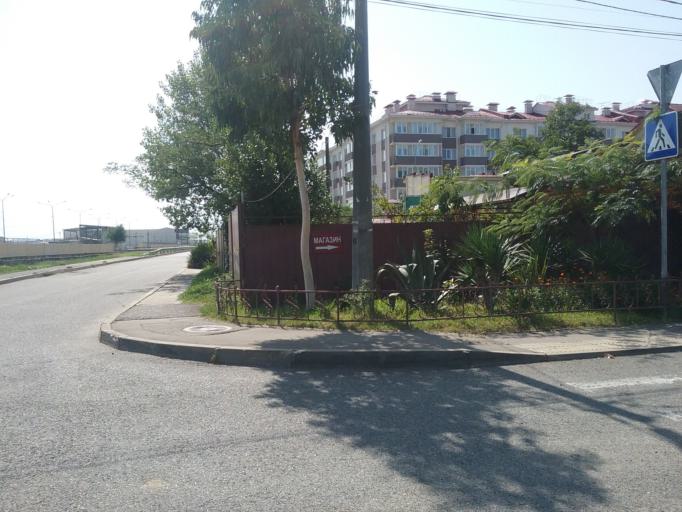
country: RU
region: Krasnodarskiy
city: Vysokoye
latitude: 43.4034
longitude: 39.9874
